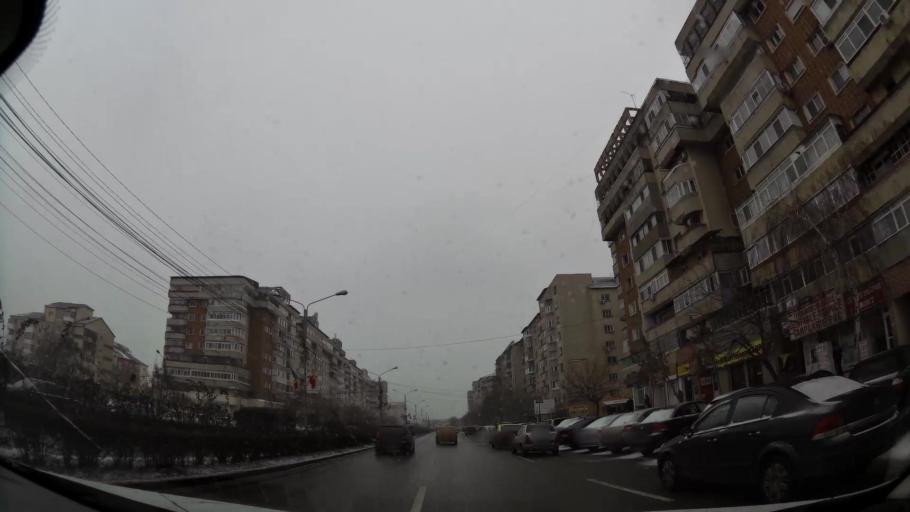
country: RO
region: Dambovita
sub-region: Municipiul Targoviste
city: Targoviste
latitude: 44.9201
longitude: 25.4770
